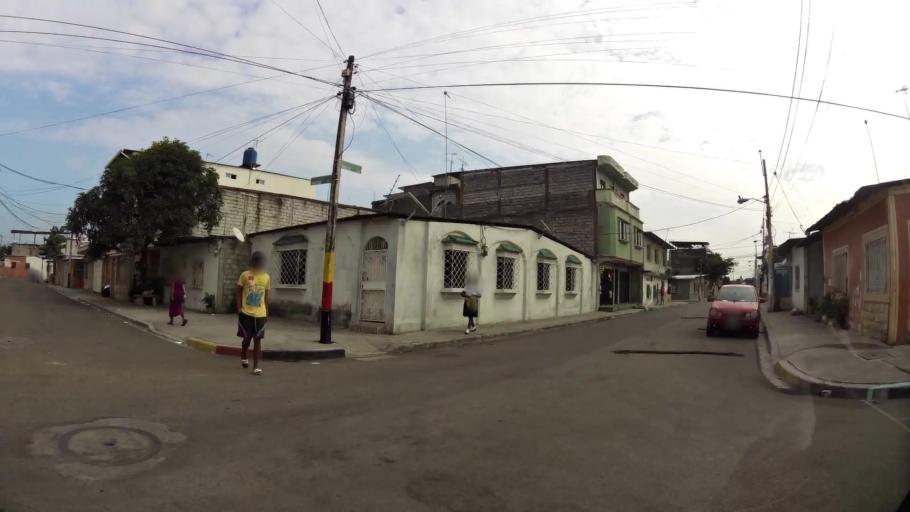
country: EC
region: Guayas
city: Guayaquil
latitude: -2.2579
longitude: -79.8867
